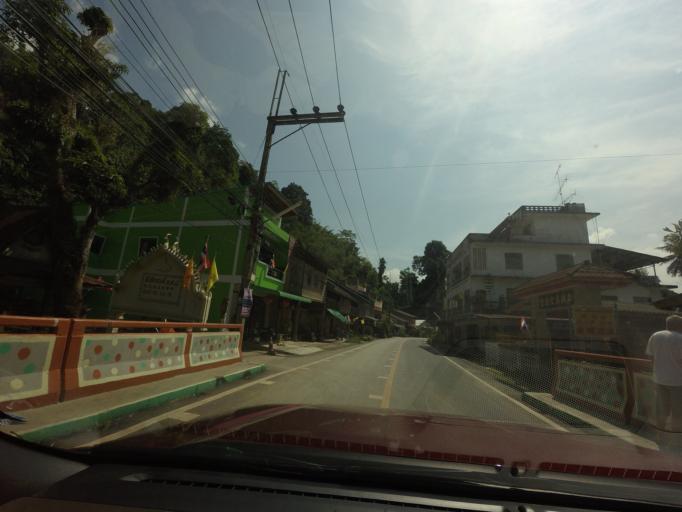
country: TH
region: Yala
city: Betong
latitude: 5.8049
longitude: 101.0712
